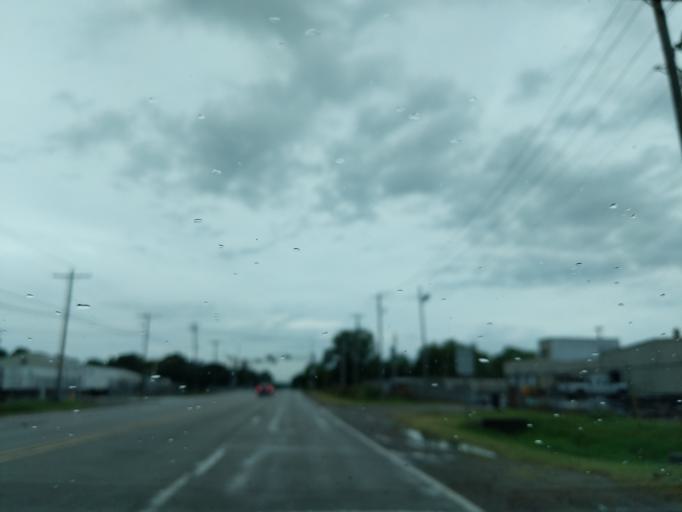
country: US
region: Illinois
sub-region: Saint Clair County
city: Fairmont City
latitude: 38.6593
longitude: -90.0785
